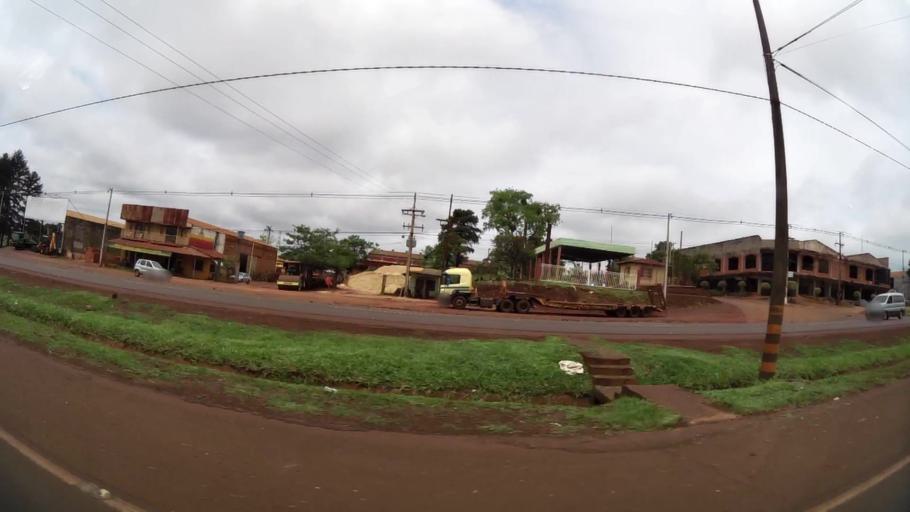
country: PY
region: Alto Parana
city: Ciudad del Este
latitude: -25.4944
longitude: -54.7037
